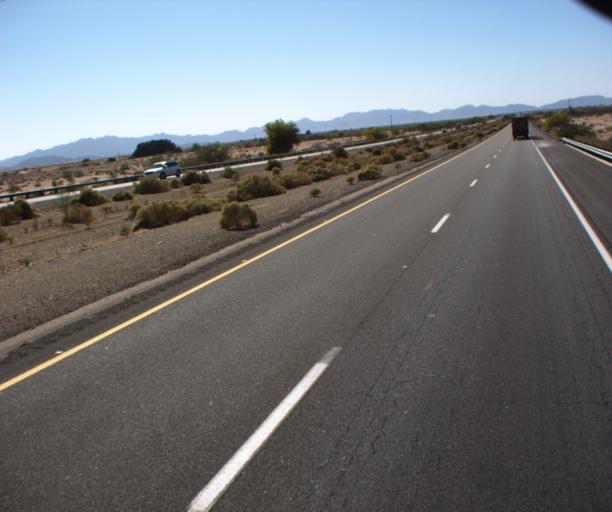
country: US
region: Arizona
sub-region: Yuma County
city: Wellton
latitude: 32.6763
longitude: -114.0520
